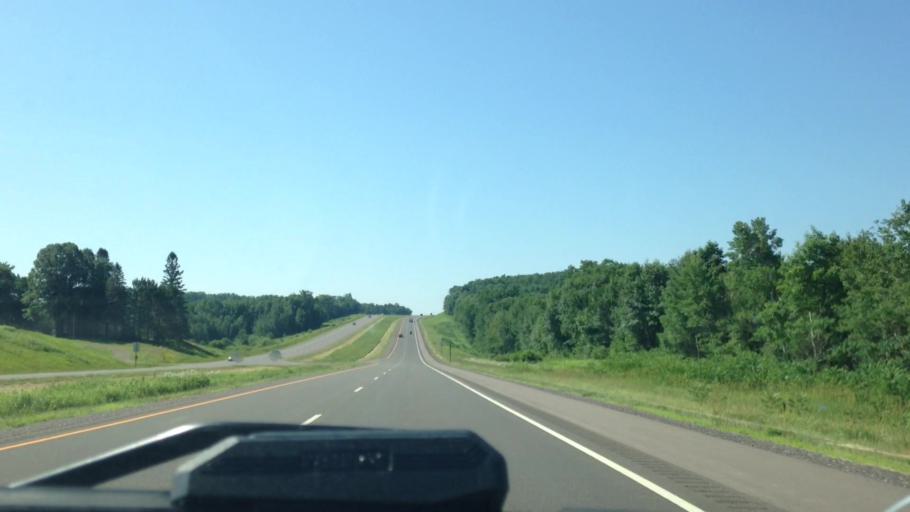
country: US
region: Wisconsin
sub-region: Washburn County
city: Spooner
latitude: 45.9797
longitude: -91.8277
